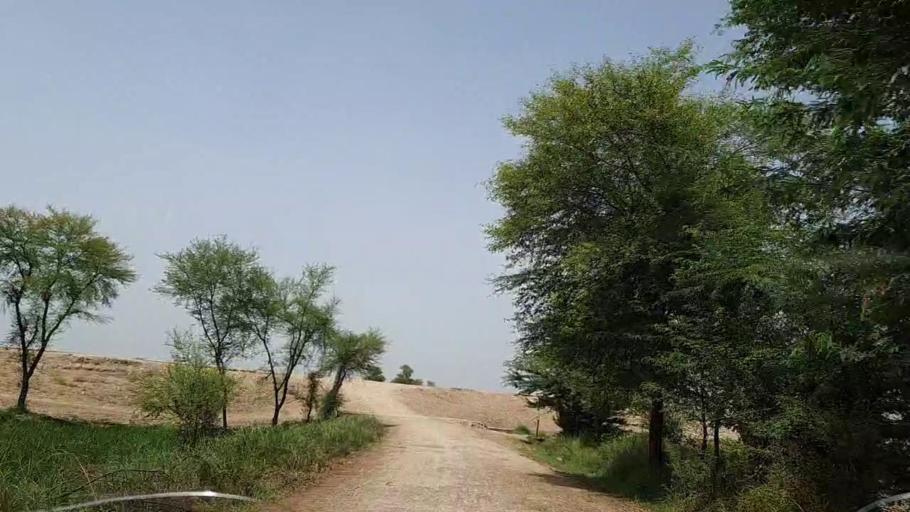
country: PK
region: Sindh
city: Tharu Shah
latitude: 26.9967
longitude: 68.0808
